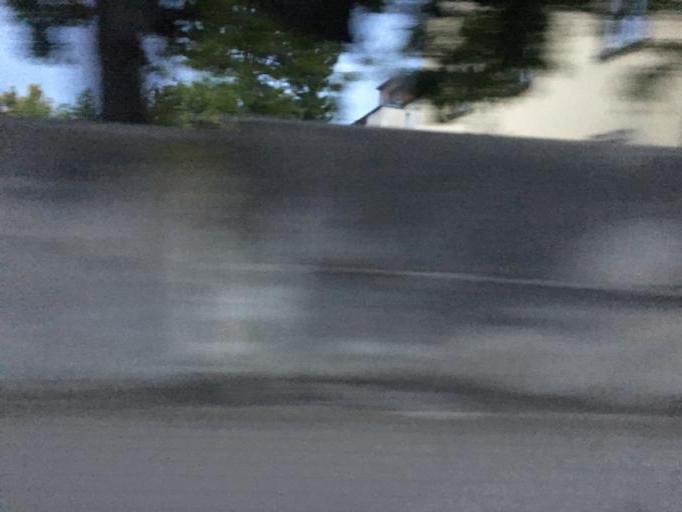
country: DE
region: Saxony
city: Wilsdruff
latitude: 51.0535
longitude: 13.5348
